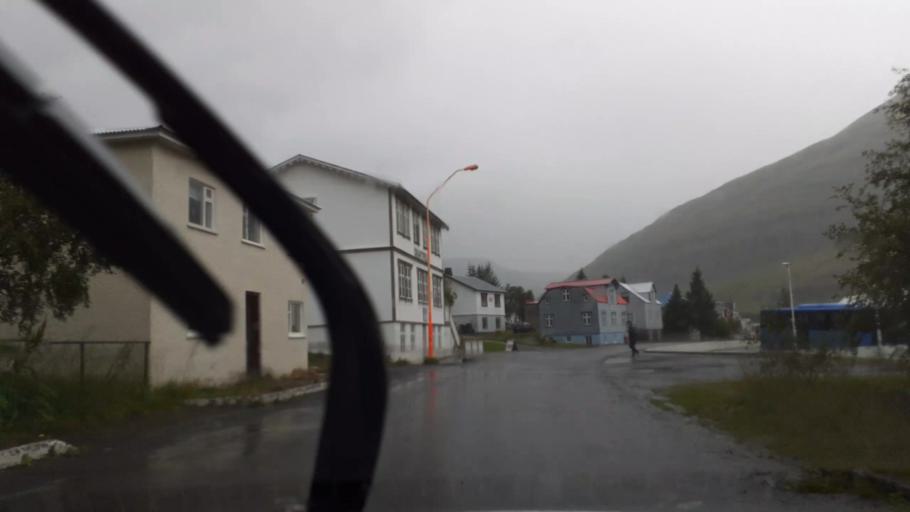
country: IS
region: East
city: Eskifjoerdur
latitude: 65.2619
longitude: -13.9974
